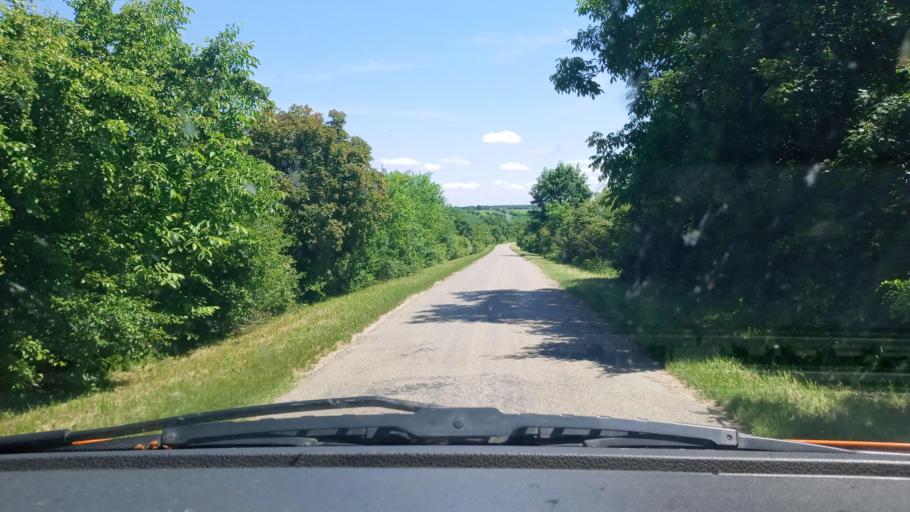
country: HU
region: Baranya
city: Szigetvar
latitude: 46.1746
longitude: 17.7464
